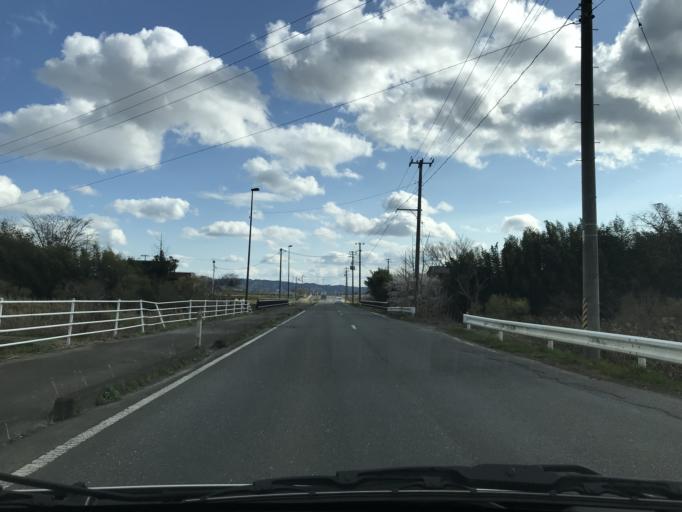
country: JP
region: Miyagi
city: Wakuya
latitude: 38.6413
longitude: 141.1884
